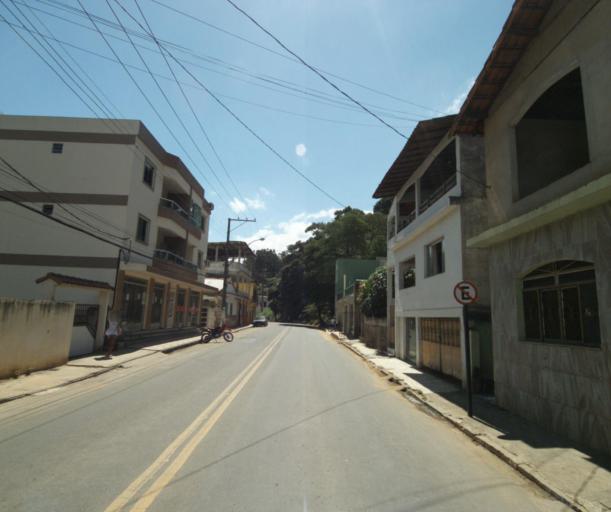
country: BR
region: Espirito Santo
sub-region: Mimoso Do Sul
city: Mimoso do Sul
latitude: -21.0669
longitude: -41.3581
